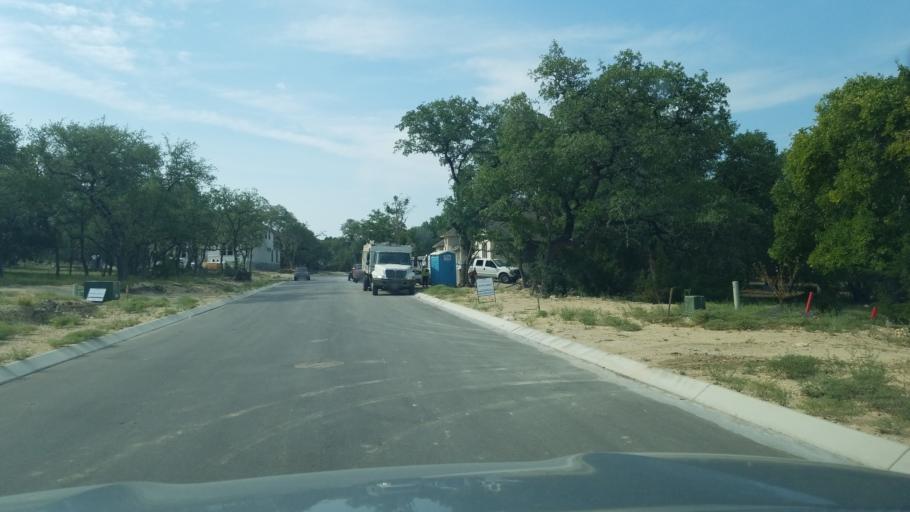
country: US
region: Texas
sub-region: Bexar County
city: Scenic Oaks
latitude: 29.7291
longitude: -98.6627
